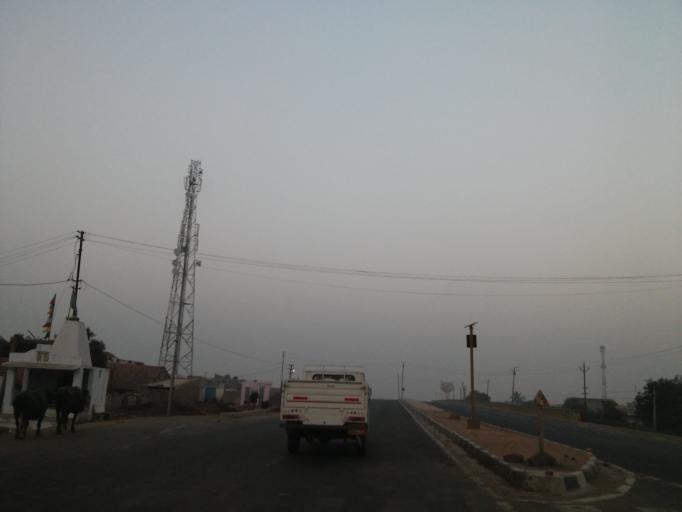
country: IN
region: Gujarat
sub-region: Surendranagar
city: Dhrangadhra
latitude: 23.0016
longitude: 71.3927
